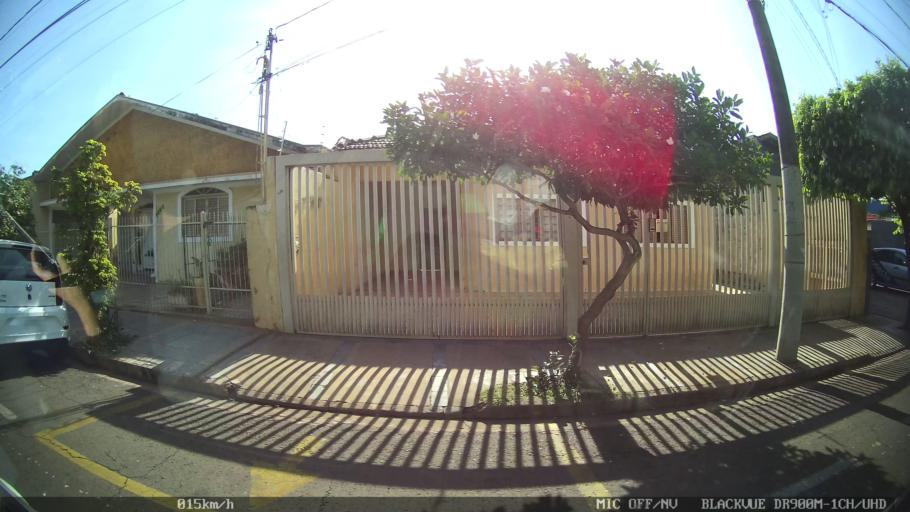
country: BR
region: Sao Paulo
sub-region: Sao Jose Do Rio Preto
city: Sao Jose do Rio Preto
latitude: -20.8071
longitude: -49.3966
